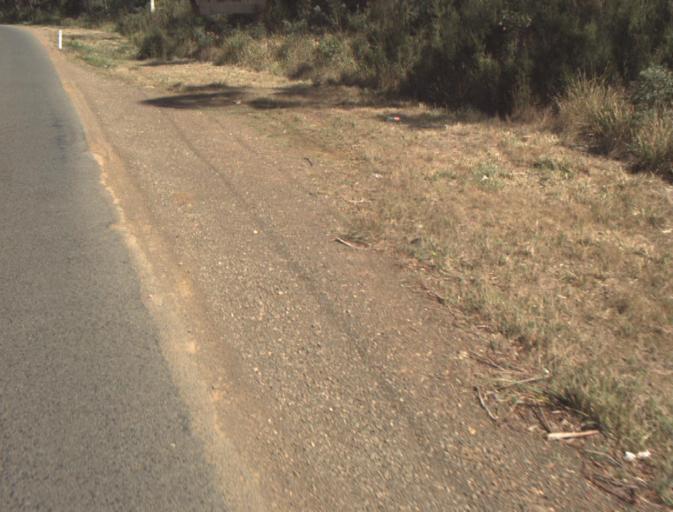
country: AU
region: Tasmania
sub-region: Launceston
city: Mayfield
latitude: -41.3327
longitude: 147.1408
